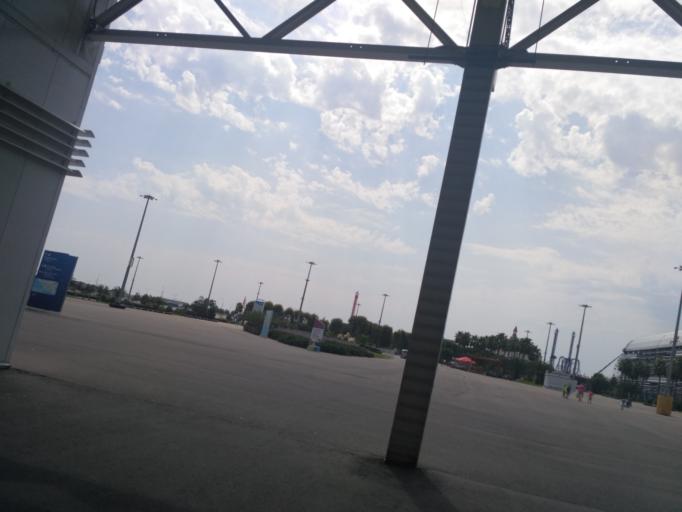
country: RU
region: Krasnodarskiy
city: Adler
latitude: 43.4105
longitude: 39.9707
